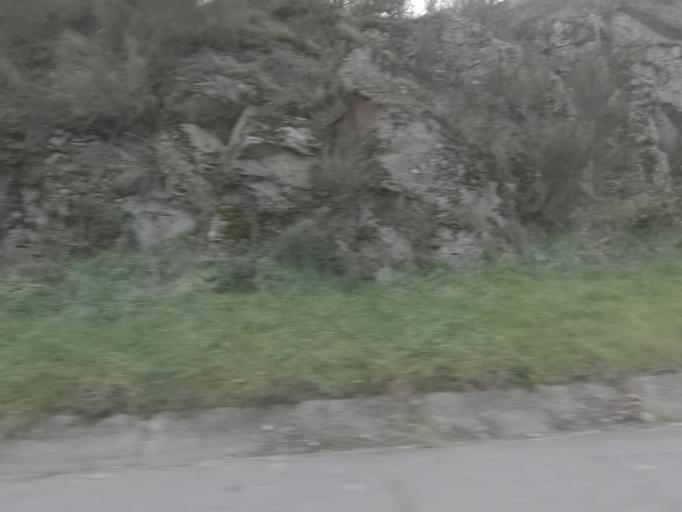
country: ES
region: Galicia
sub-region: Provincia de Ourense
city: Allariz
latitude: 42.1948
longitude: -7.7978
